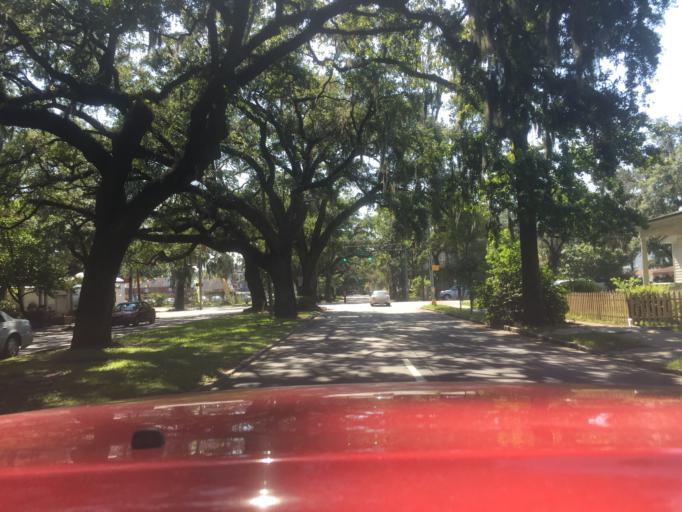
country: US
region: Georgia
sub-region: Chatham County
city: Savannah
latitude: 32.0587
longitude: -81.1063
